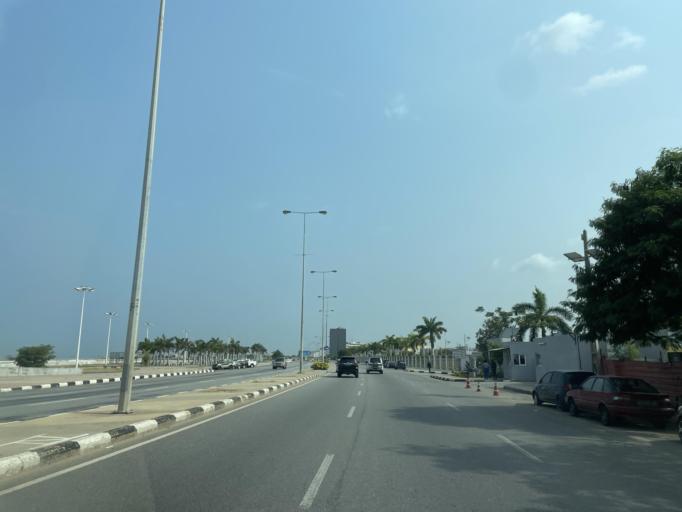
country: AO
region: Luanda
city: Luanda
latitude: -8.8251
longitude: 13.2155
